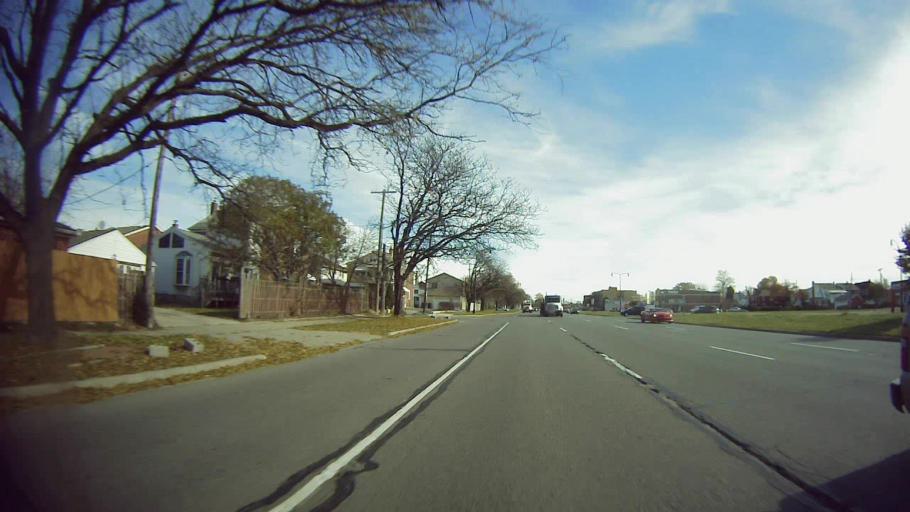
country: US
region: Michigan
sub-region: Wayne County
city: Dearborn
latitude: 42.3297
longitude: -83.1818
